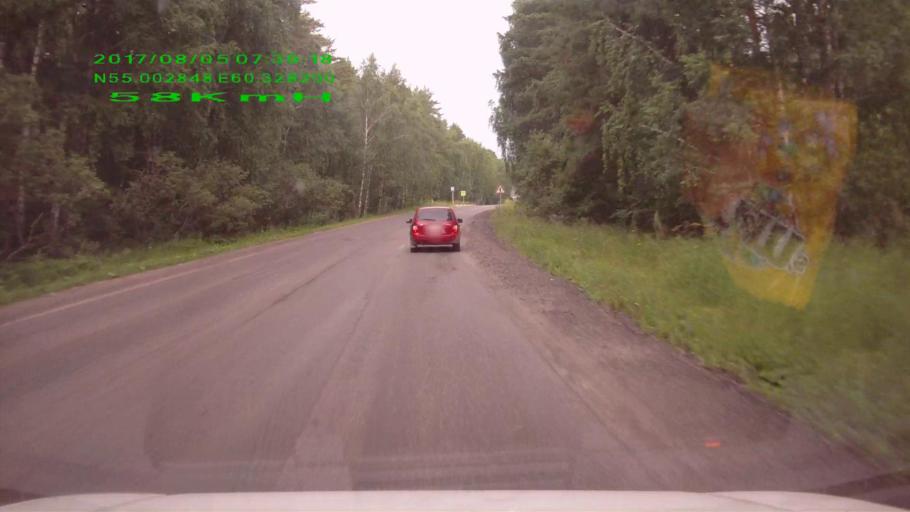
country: RU
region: Chelyabinsk
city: Chebarkul'
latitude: 55.0029
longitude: 60.3278
